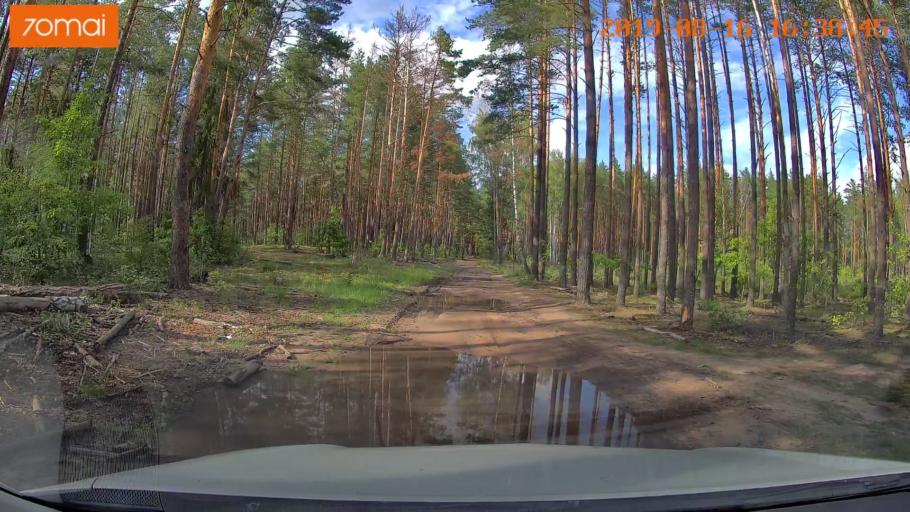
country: BY
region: Mogilev
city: Asipovichy
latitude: 53.2344
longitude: 28.7774
